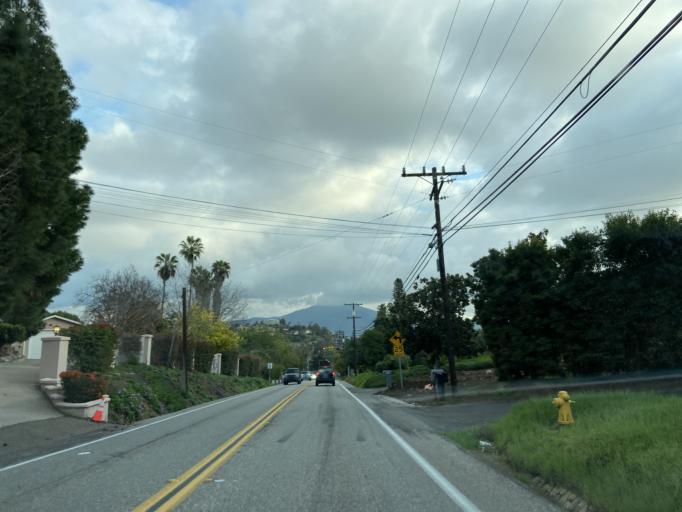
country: US
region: California
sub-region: San Diego County
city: Casa de Oro-Mount Helix
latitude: 32.7680
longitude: -116.9733
